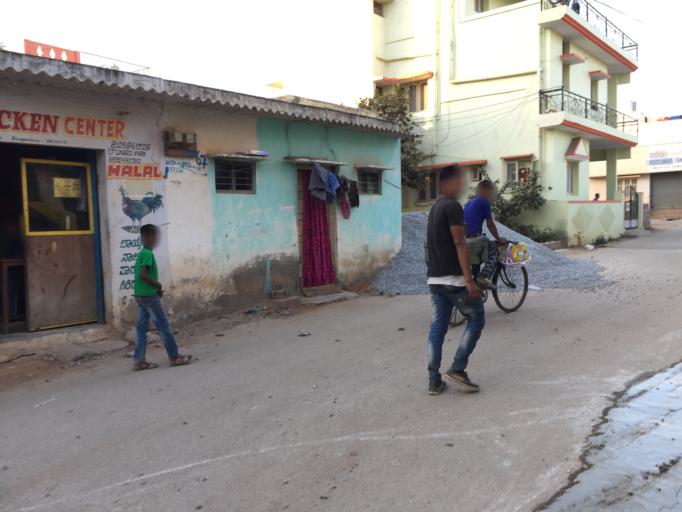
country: IN
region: Karnataka
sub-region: Bangalore Urban
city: Yelahanka
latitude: 13.0527
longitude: 77.6282
